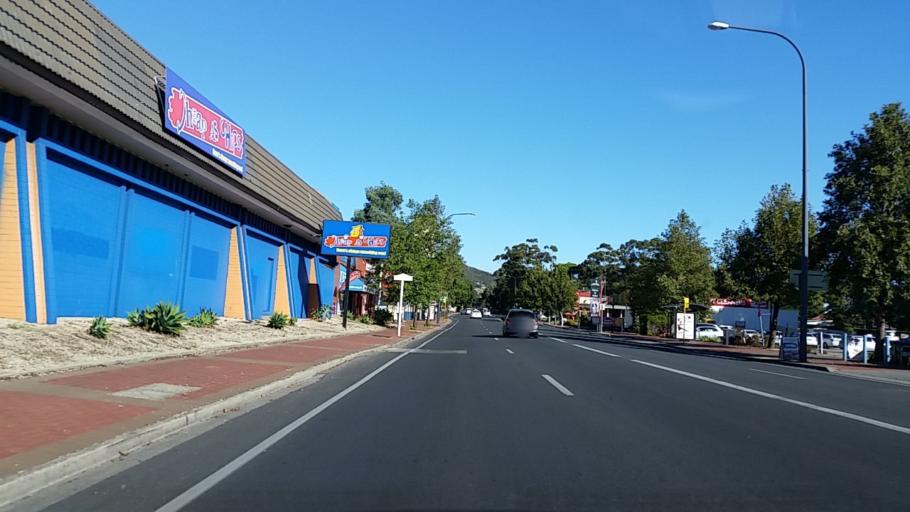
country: AU
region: South Australia
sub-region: Mitcham
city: Hawthorn
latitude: -34.9745
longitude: 138.6093
